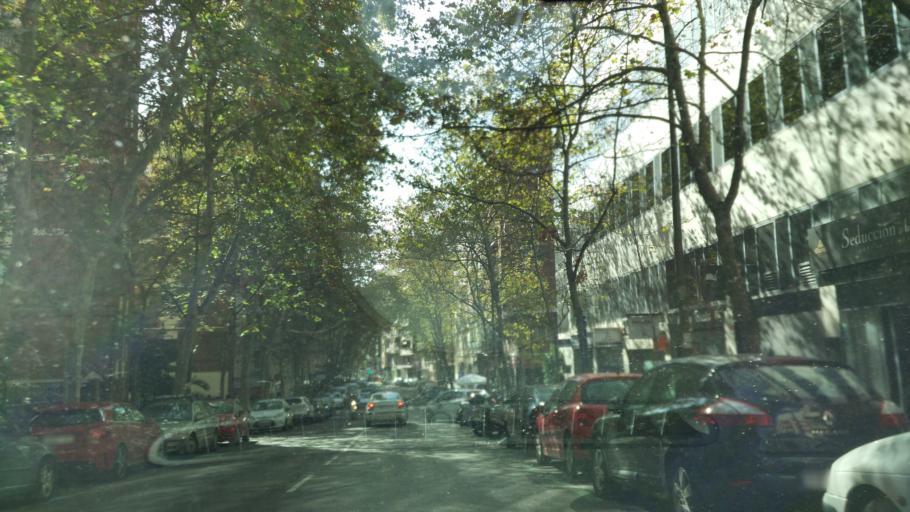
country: ES
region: Madrid
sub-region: Provincia de Madrid
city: Tetuan de las Victorias
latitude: 40.4550
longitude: -3.6987
